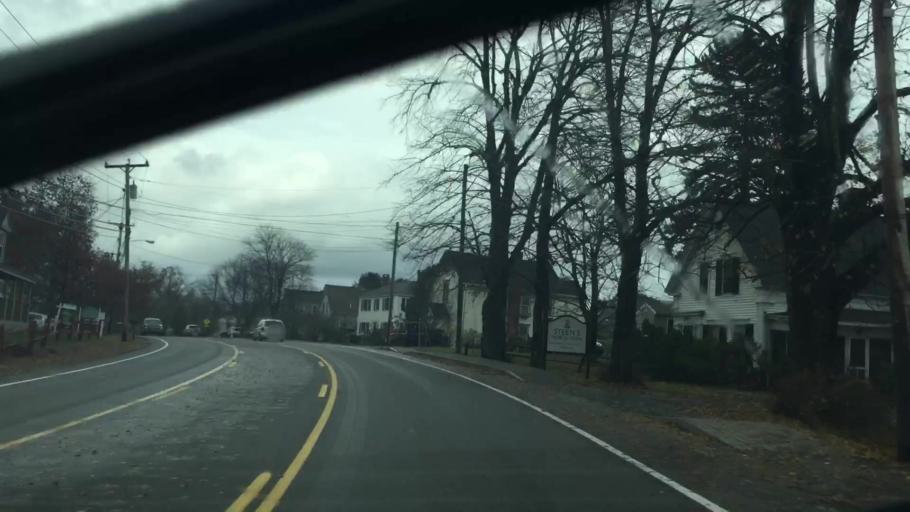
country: US
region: Maine
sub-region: York County
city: Wells Beach Station
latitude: 43.3288
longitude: -70.5742
